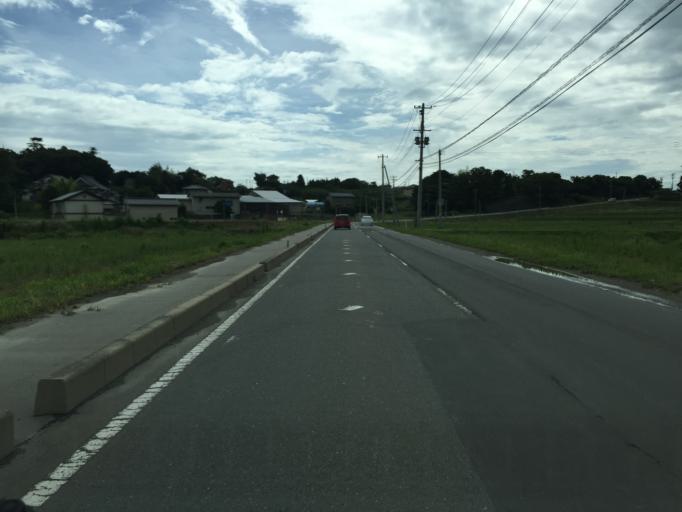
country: JP
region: Miyagi
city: Marumori
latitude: 37.7652
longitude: 140.9875
